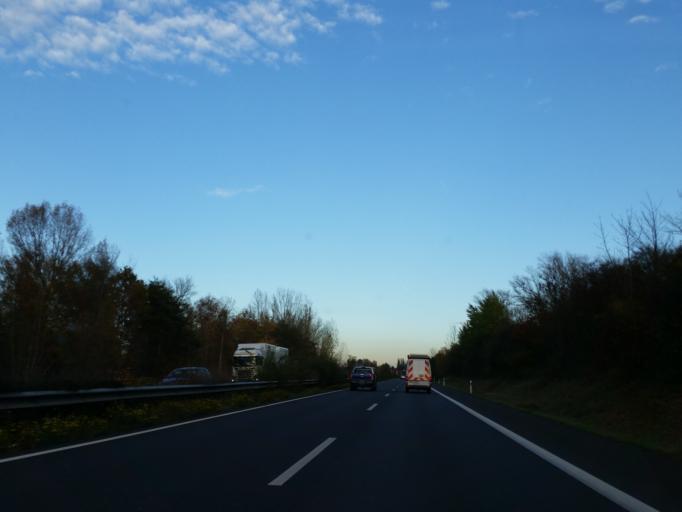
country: DE
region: Lower Saxony
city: Braunschweig
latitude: 52.2421
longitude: 10.5483
